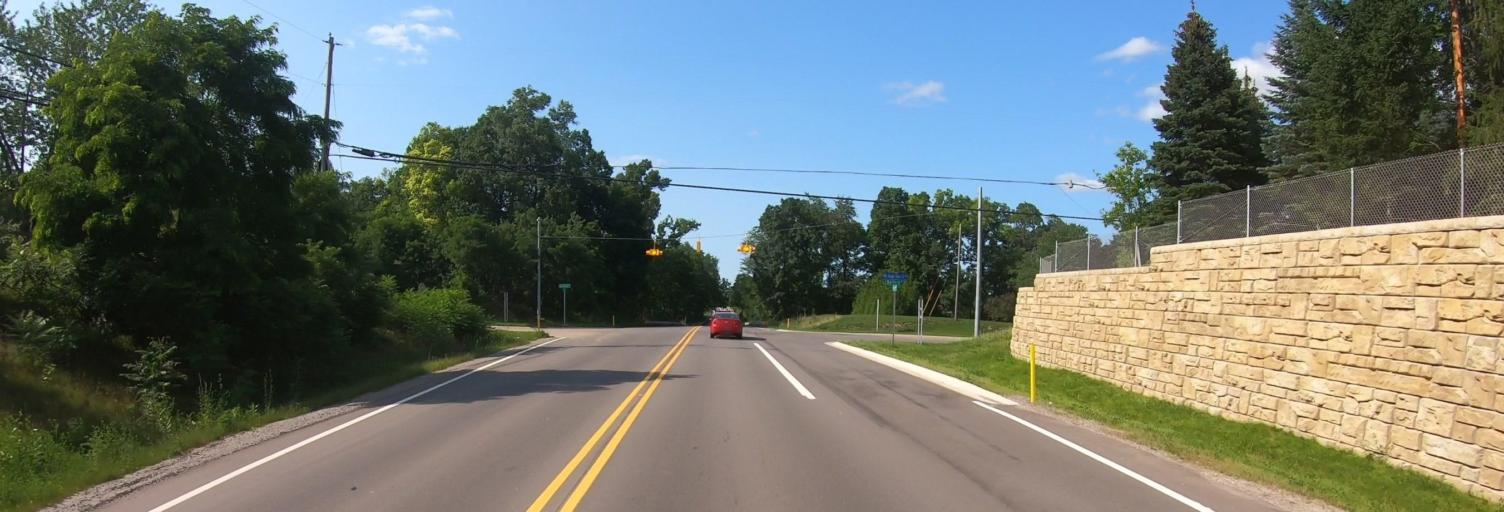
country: US
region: Michigan
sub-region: Genesee County
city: Grand Blanc
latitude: 42.8600
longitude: -83.6301
